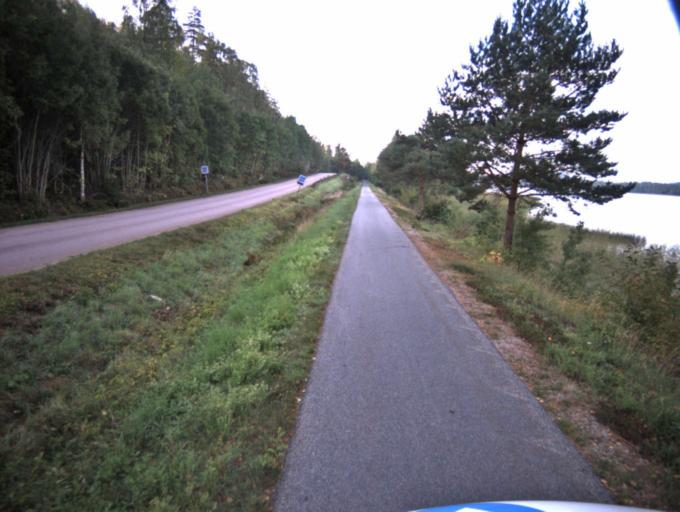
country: SE
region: Vaestra Goetaland
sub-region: Ulricehamns Kommun
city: Ulricehamn
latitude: 57.7507
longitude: 13.3942
